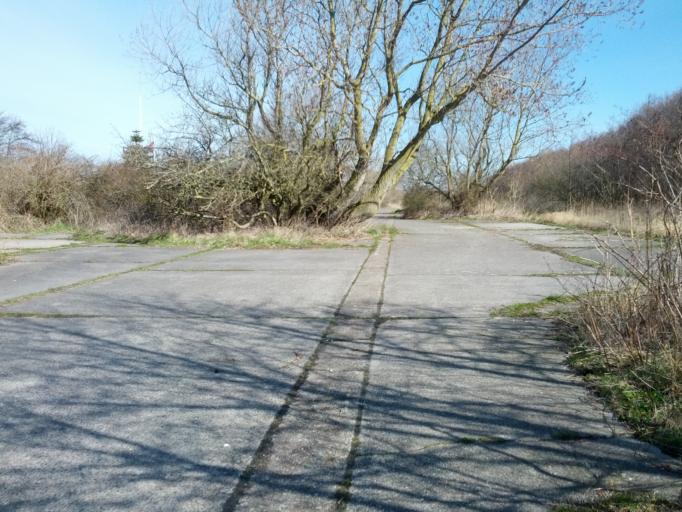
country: DE
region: Lower Saxony
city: Langeoog
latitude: 53.7391
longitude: 7.4742
